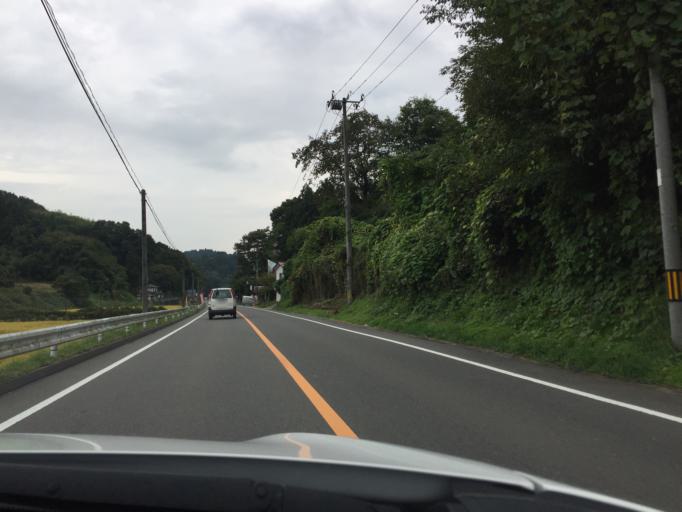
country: JP
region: Fukushima
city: Nihommatsu
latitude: 37.5996
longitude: 140.5362
